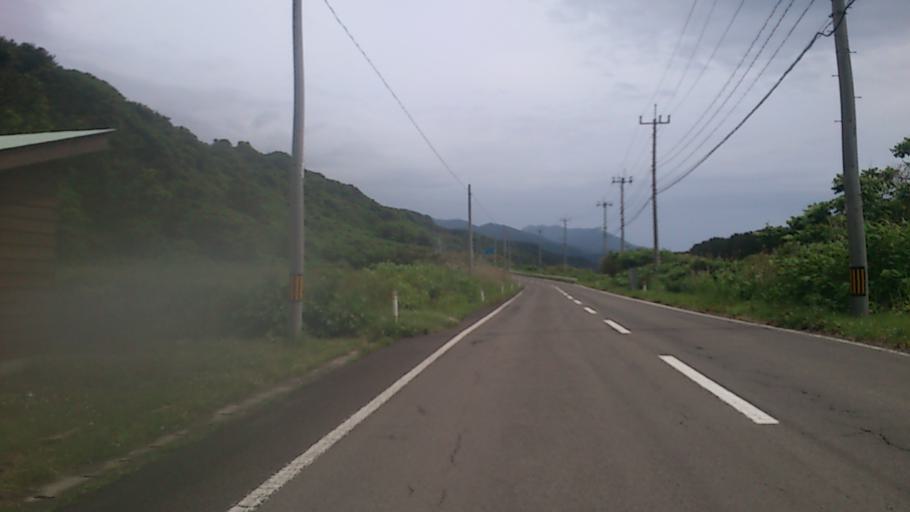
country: JP
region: Akita
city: Noshiromachi
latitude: 40.5269
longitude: 139.9492
